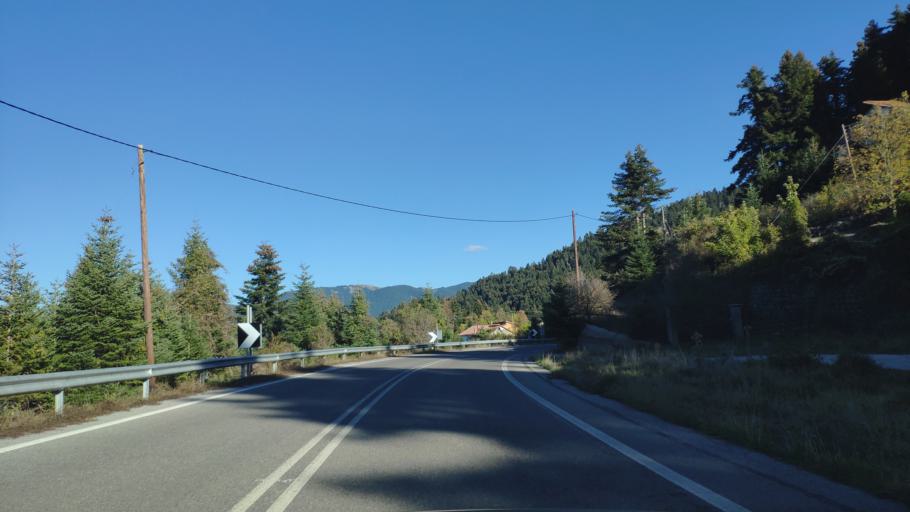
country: GR
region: Peloponnese
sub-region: Nomos Arkadias
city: Langadhia
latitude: 37.6566
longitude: 22.1279
